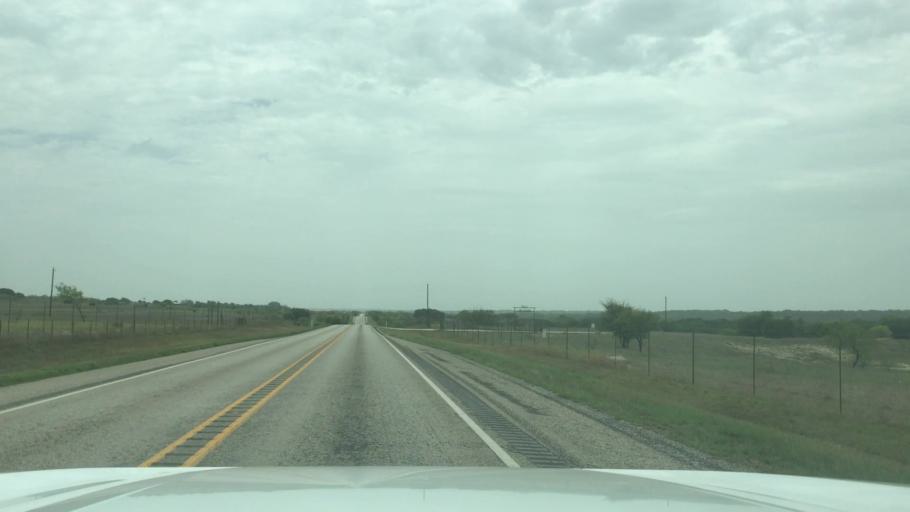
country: US
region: Texas
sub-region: Hamilton County
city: Hico
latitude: 32.0535
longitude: -98.1730
